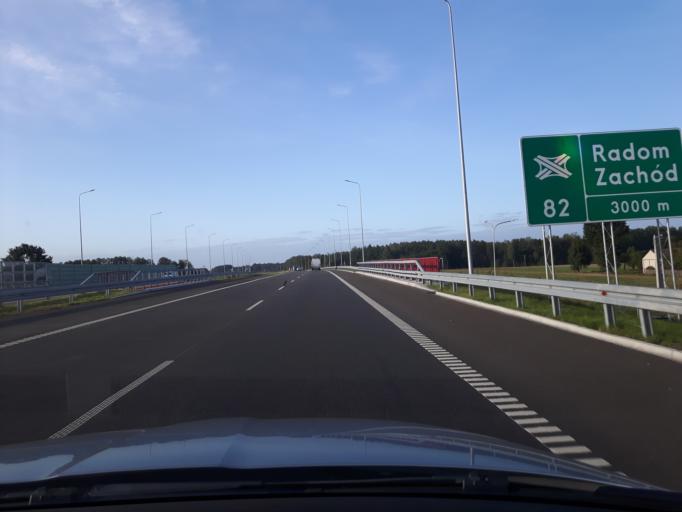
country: PL
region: Masovian Voivodeship
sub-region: Powiat radomski
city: Zakrzew
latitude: 51.4514
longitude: 21.0378
